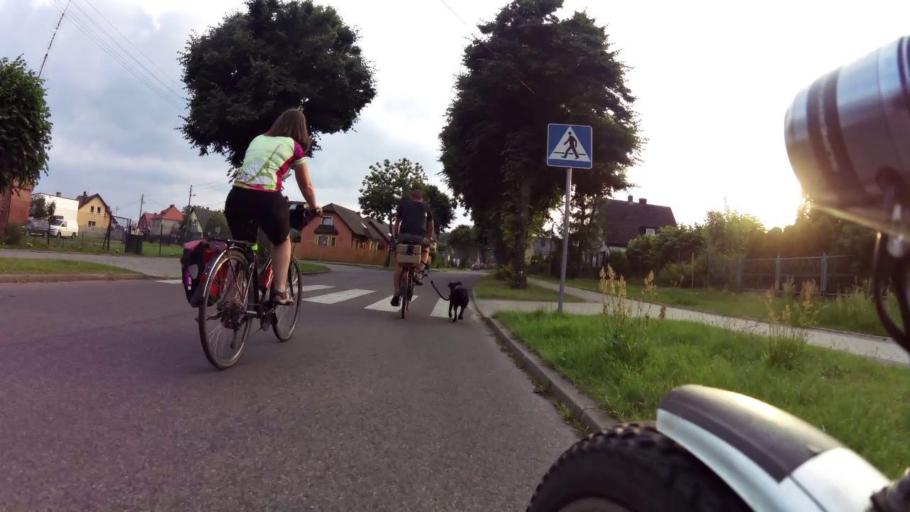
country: PL
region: West Pomeranian Voivodeship
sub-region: Powiat goleniowski
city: Stepnica
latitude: 53.6616
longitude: 14.4974
